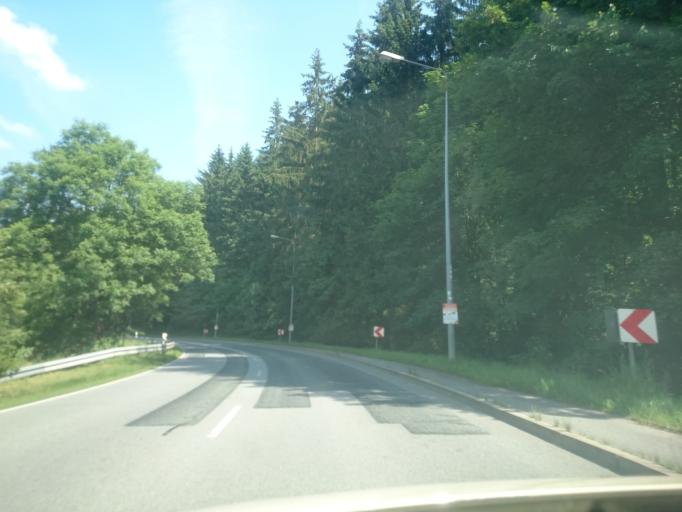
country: DE
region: Saxony
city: Marienberg
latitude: 50.6548
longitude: 13.1789
